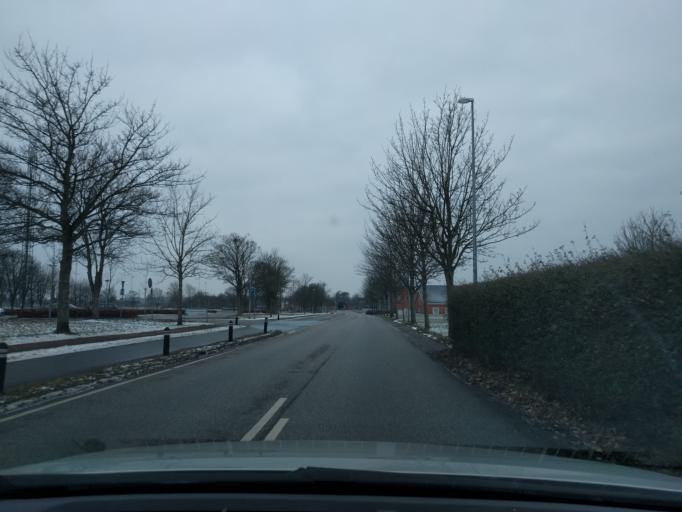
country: DK
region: South Denmark
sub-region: Middelfart Kommune
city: Middelfart
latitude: 55.4958
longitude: 9.7487
